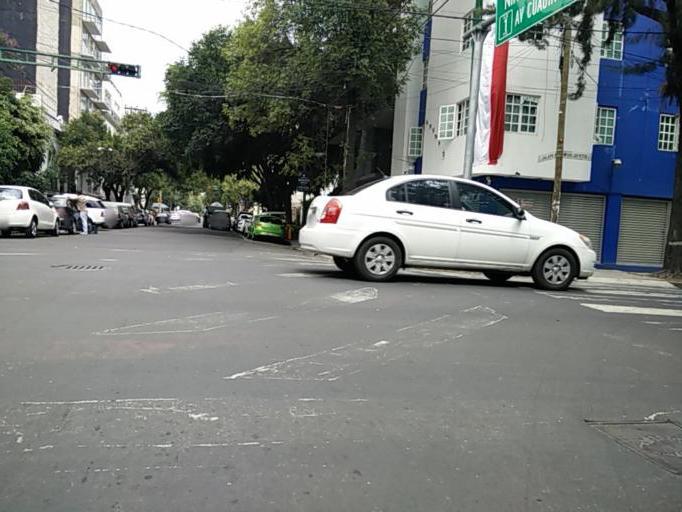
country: MX
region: Mexico City
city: Benito Juarez
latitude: 19.4141
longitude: -99.1600
